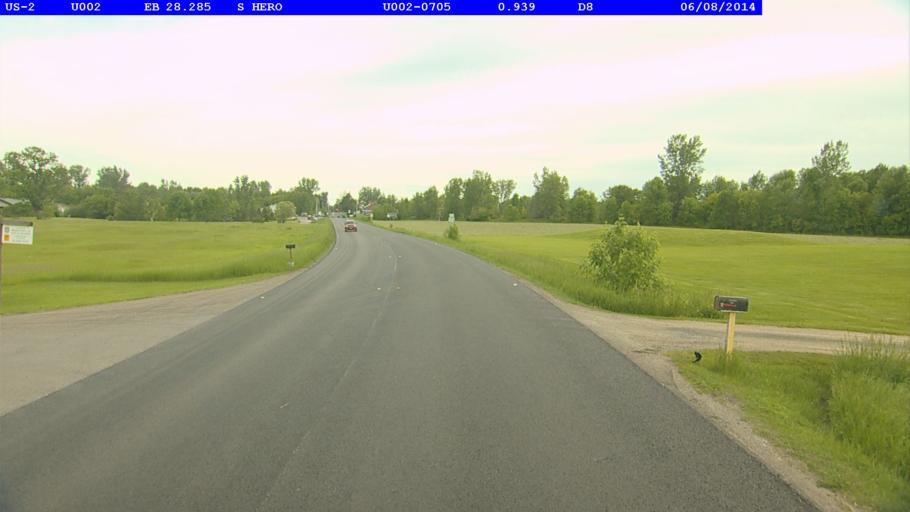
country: US
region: New York
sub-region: Clinton County
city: Cumberland Head
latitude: 44.6676
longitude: -73.3229
